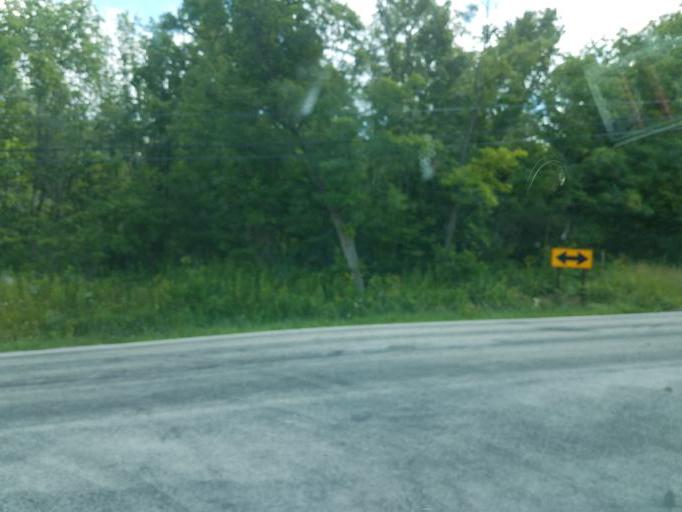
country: US
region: Ohio
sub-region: Richland County
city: Ontario
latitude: 40.7394
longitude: -82.6233
